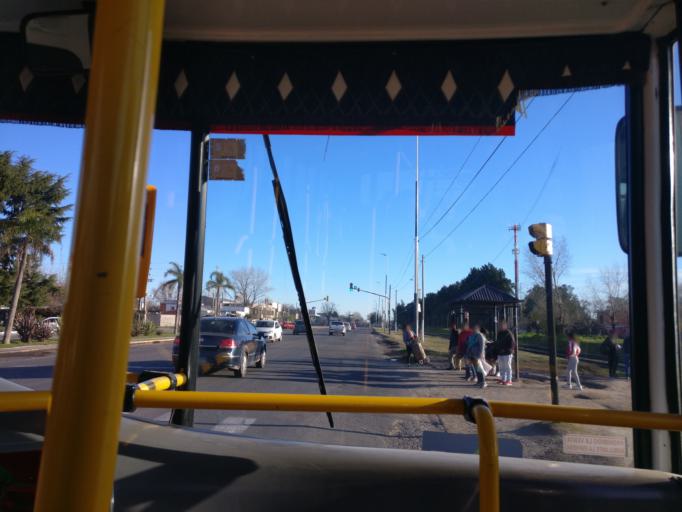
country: AR
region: Buenos Aires
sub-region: Partido de Ezeiza
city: Ezeiza
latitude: -34.8970
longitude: -58.5772
